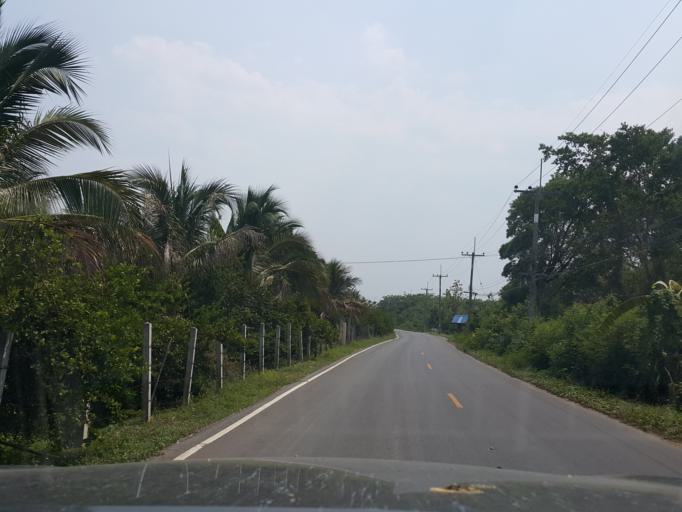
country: TH
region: Lampang
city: Mae Phrik
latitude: 17.5053
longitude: 99.1310
